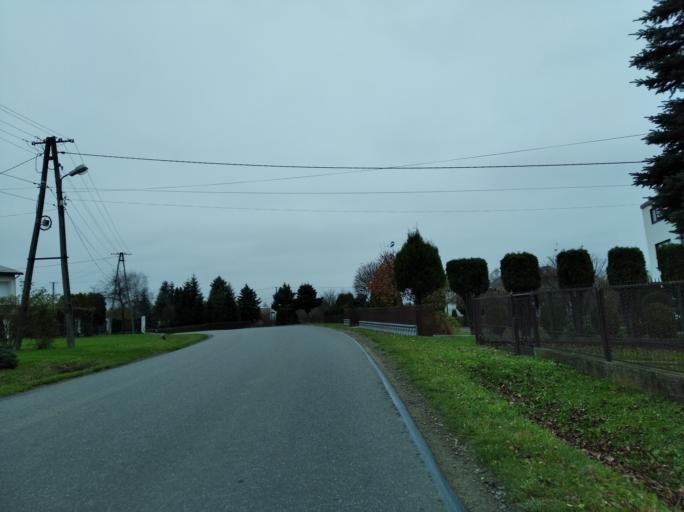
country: PL
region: Subcarpathian Voivodeship
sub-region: Powiat krosnienski
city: Chorkowka
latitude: 49.6731
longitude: 21.6829
